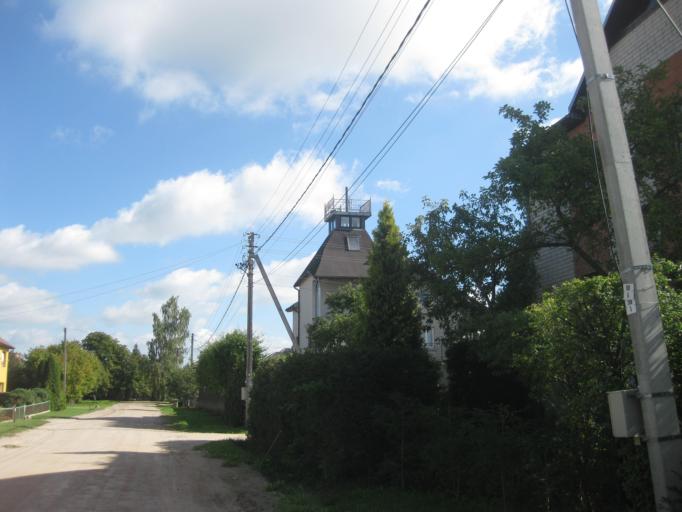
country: LT
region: Kauno apskritis
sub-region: Kauno rajonas
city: Garliava
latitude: 54.8261
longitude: 23.8812
